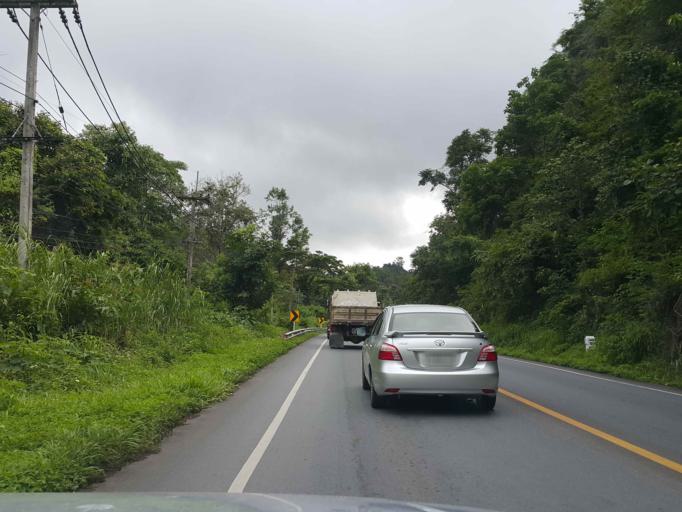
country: TH
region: Tak
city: Tak
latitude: 16.7985
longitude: 98.9523
